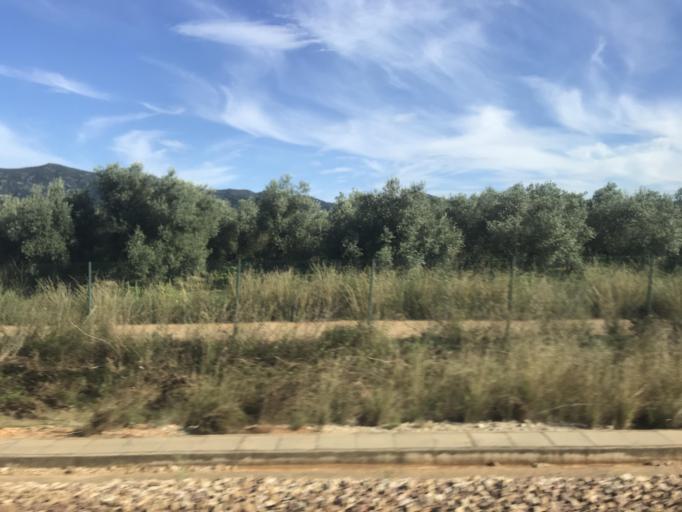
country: ES
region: Catalonia
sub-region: Provincia de Tarragona
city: Ulldecona
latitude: 40.6169
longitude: 0.4720
